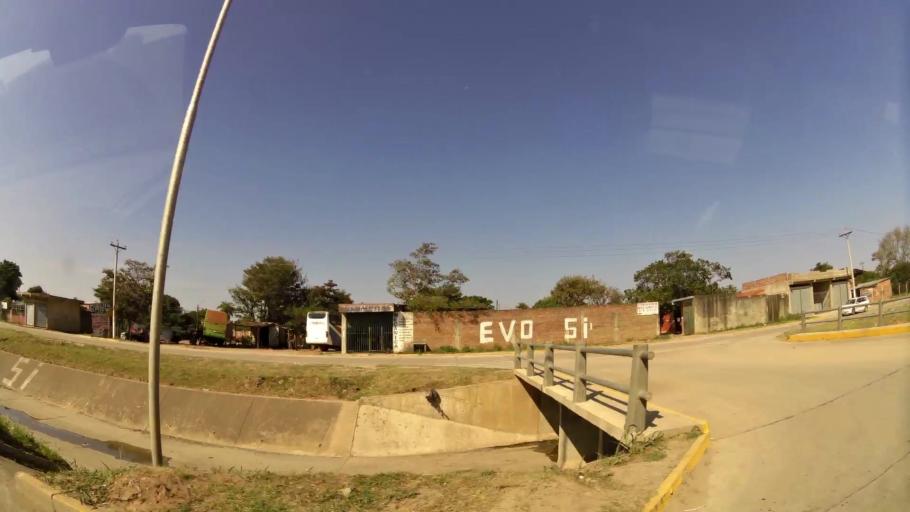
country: BO
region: Santa Cruz
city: Cotoca
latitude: -17.8104
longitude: -63.1097
